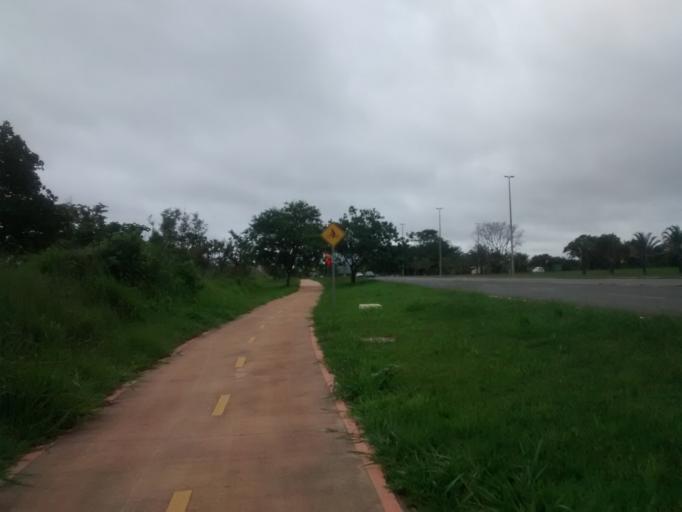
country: BR
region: Federal District
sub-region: Brasilia
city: Brasilia
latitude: -15.8035
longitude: -47.8510
